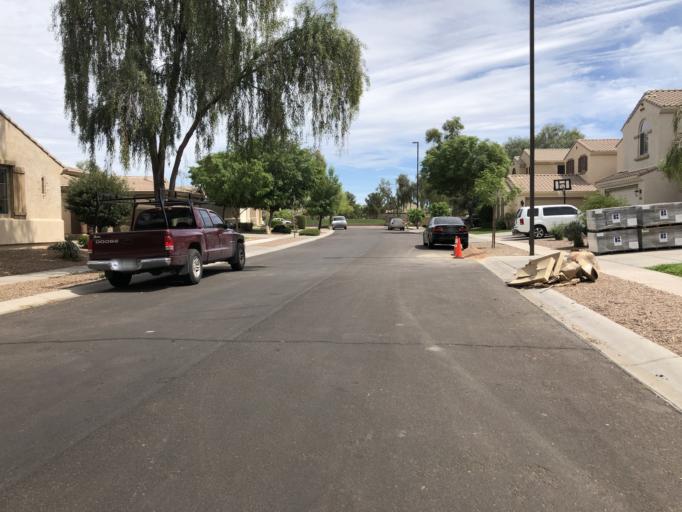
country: US
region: Arizona
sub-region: Maricopa County
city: Queen Creek
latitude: 33.2717
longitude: -111.6876
